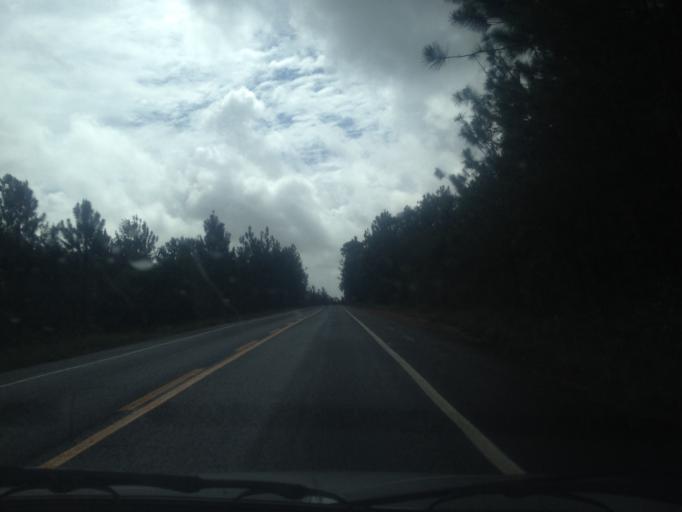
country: BR
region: Bahia
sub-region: Conde
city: Conde
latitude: -12.1071
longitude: -37.7838
